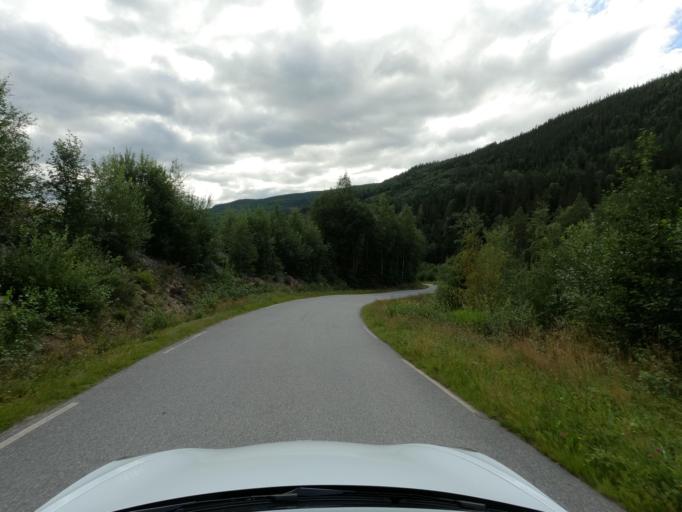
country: NO
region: Telemark
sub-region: Tinn
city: Rjukan
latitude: 59.9922
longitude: 8.6983
